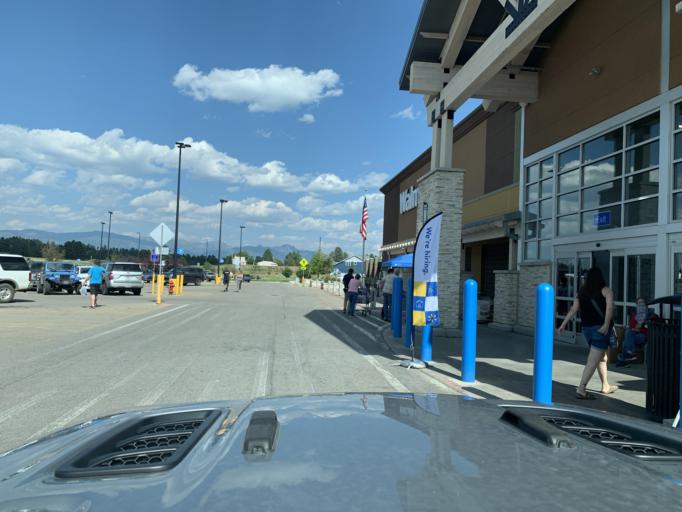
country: US
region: Colorado
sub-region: Archuleta County
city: Pagosa Springs
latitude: 37.2600
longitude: -107.0634
